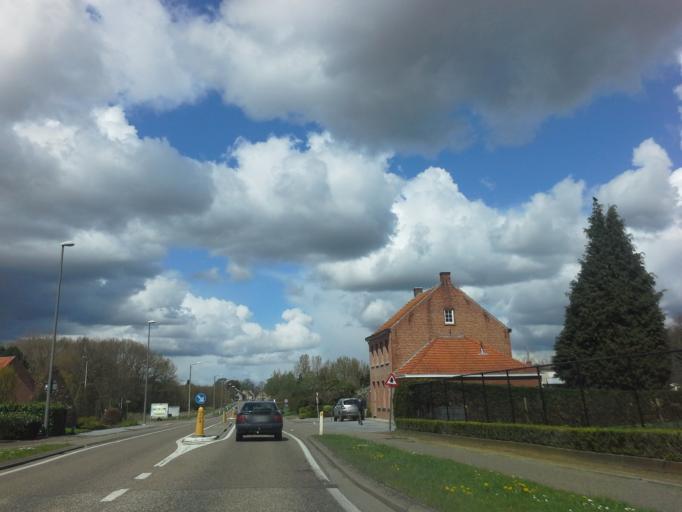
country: BE
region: Flanders
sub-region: Provincie Limburg
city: Tessenderlo
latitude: 51.0788
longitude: 5.0765
